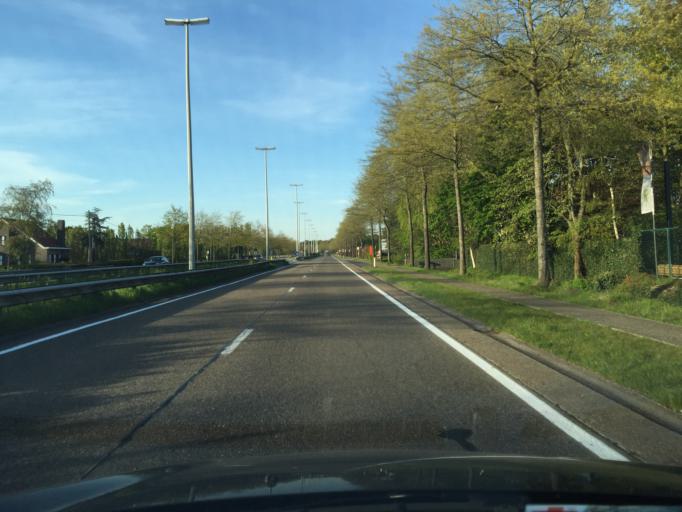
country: BE
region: Flanders
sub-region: Provincie Oost-Vlaanderen
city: Knesselare
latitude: 51.1640
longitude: 3.4401
